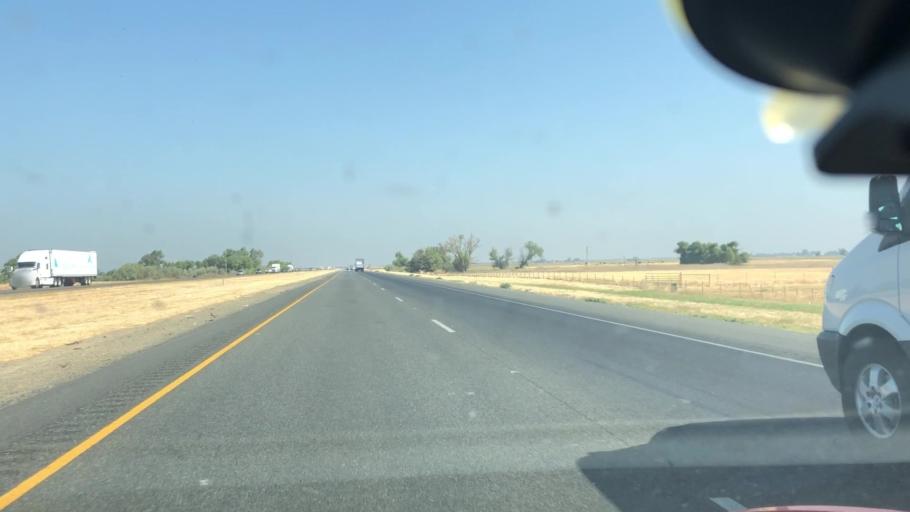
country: US
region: California
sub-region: Sacramento County
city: Laguna
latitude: 38.3419
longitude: -121.4697
